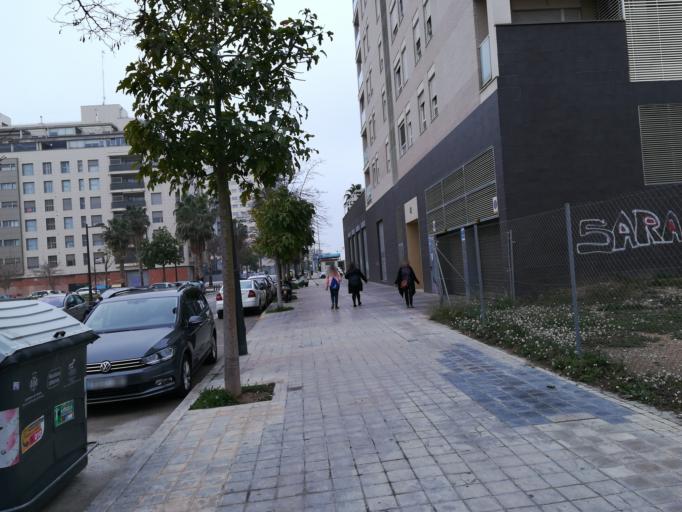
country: ES
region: Valencia
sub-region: Provincia de Valencia
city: Mislata
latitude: 39.4880
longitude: -0.4028
